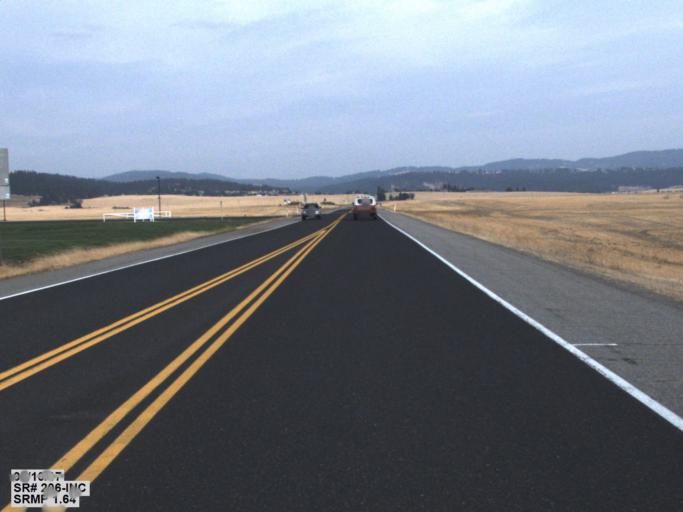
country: US
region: Washington
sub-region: Spokane County
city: Mead
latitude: 47.7875
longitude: -117.3197
